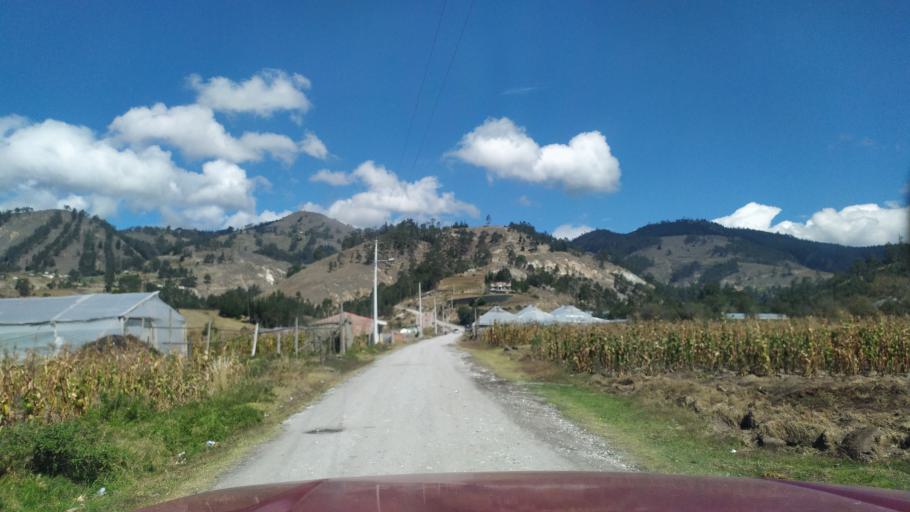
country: EC
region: Chimborazo
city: Riobamba
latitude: -1.6805
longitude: -78.6877
